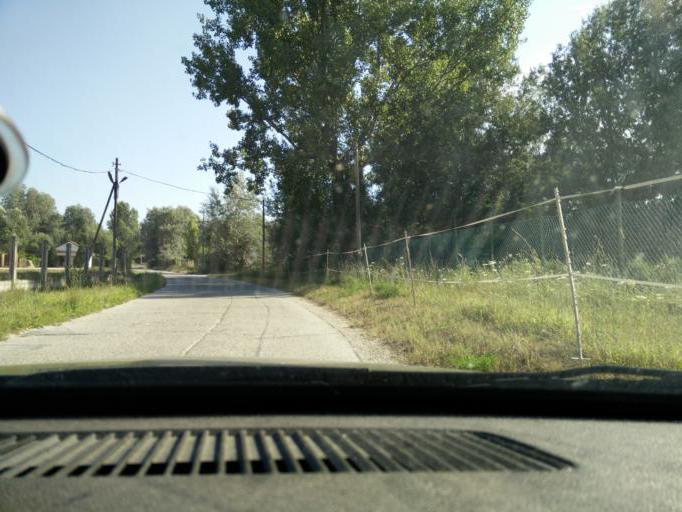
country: HU
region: Komarom-Esztergom
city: Tatabanya
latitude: 47.5572
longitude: 18.4468
